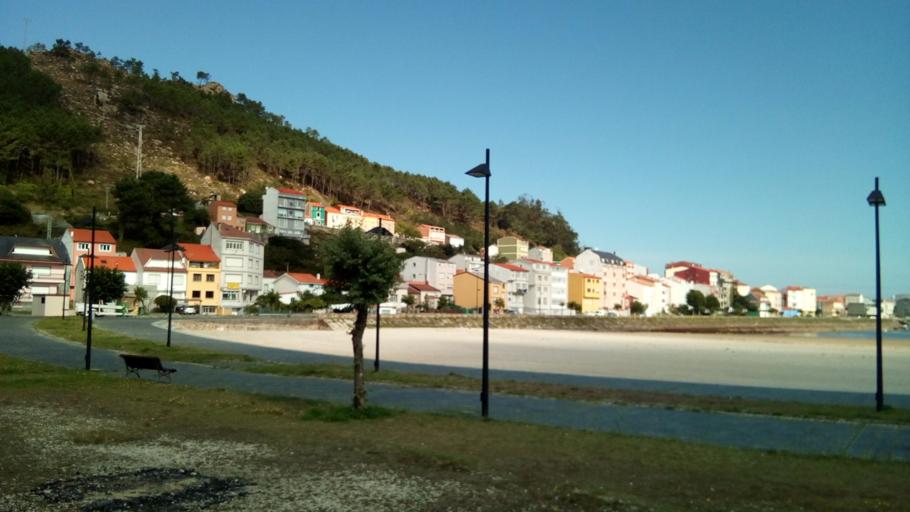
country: ES
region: Galicia
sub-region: Provincia da Coruna
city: Vimianzo
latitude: 43.1788
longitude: -9.0912
